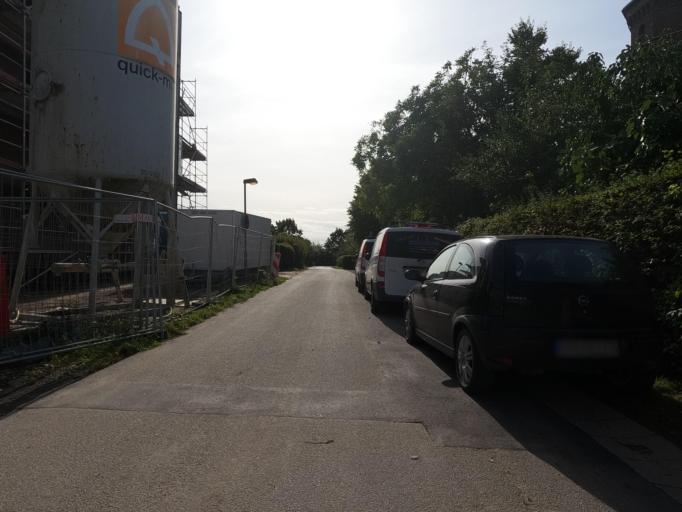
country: DE
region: Schleswig-Holstein
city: Dahme
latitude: 54.2021
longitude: 11.0905
